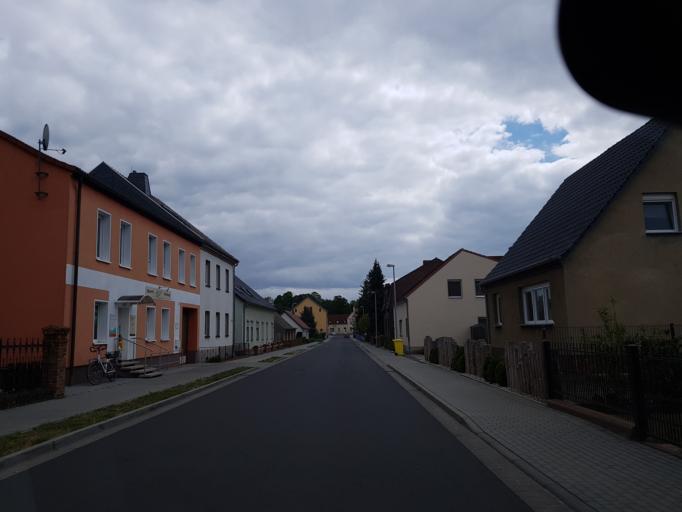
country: DE
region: Brandenburg
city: Altdobern
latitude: 51.6509
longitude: 14.0290
